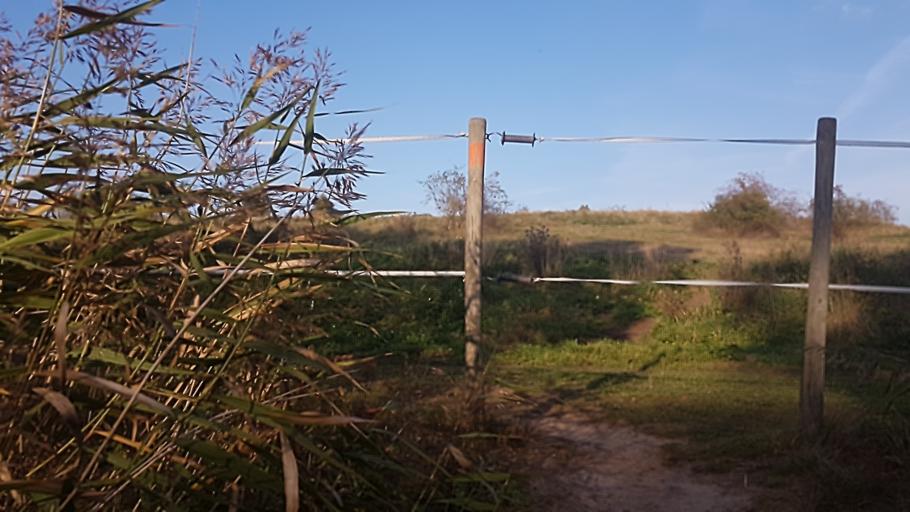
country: SE
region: Kalmar
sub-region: Kalmar Kommun
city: Rinkabyholm
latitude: 56.6602
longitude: 16.3038
